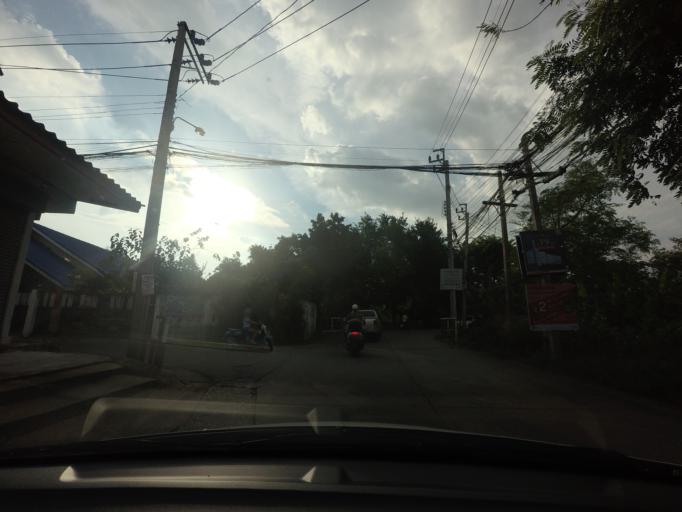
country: TH
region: Bangkok
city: Lak Si
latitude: 13.8922
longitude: 100.5784
